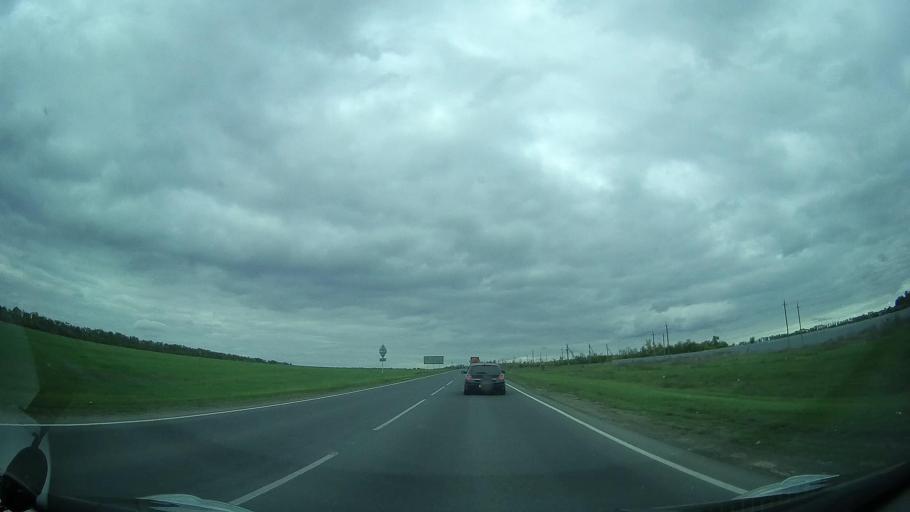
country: RU
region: Rostov
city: Yegorlykskaya
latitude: 46.5688
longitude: 40.6302
